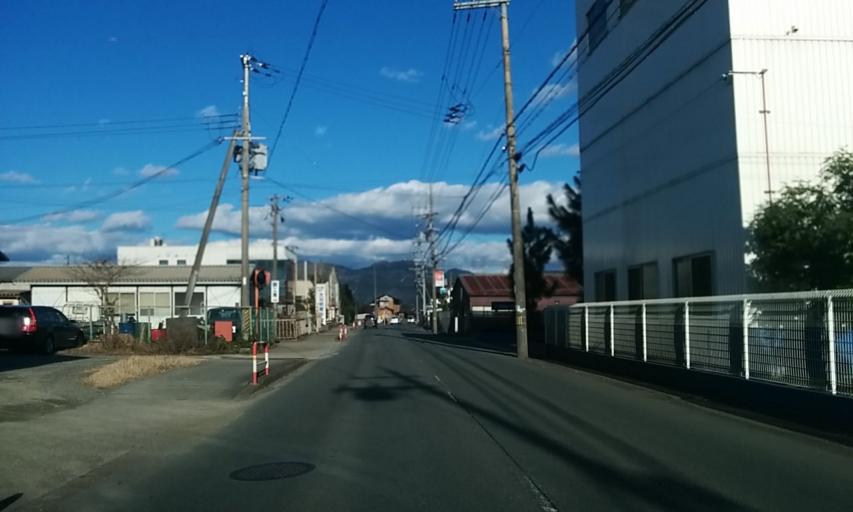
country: JP
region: Kyoto
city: Fukuchiyama
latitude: 35.2938
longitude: 135.0866
